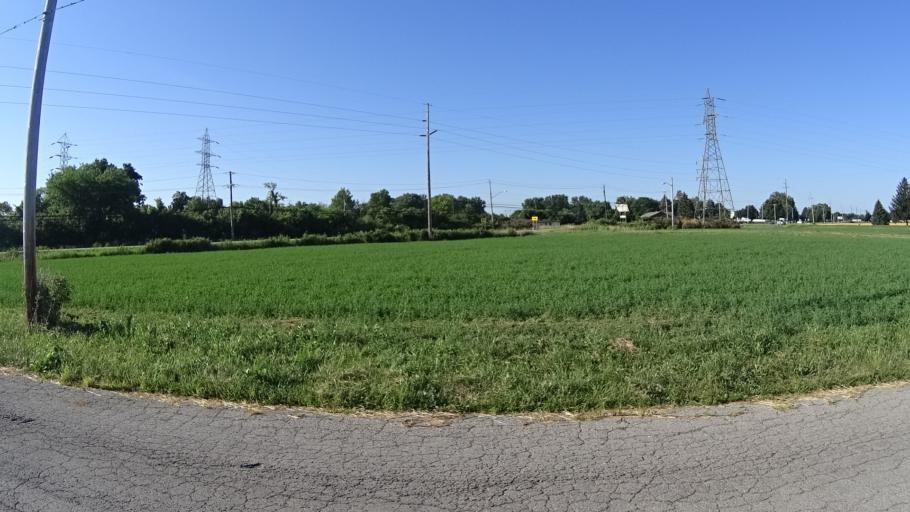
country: US
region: Ohio
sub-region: Erie County
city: Sandusky
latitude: 41.4338
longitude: -82.7425
